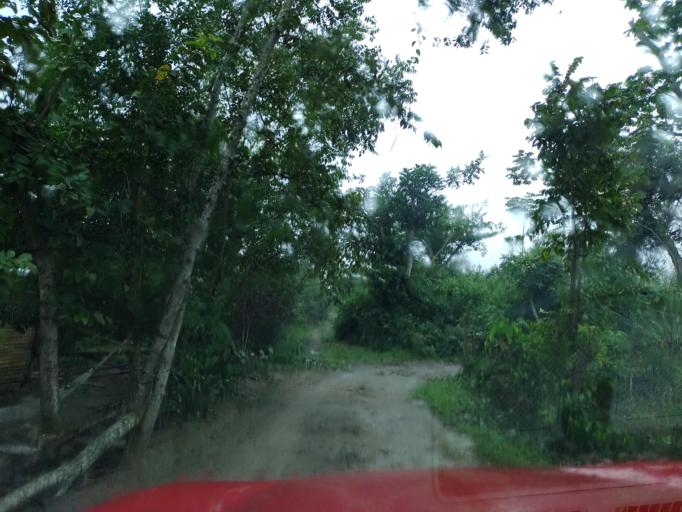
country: MX
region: Veracruz
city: Agua Dulce
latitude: 20.3353
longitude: -97.3171
